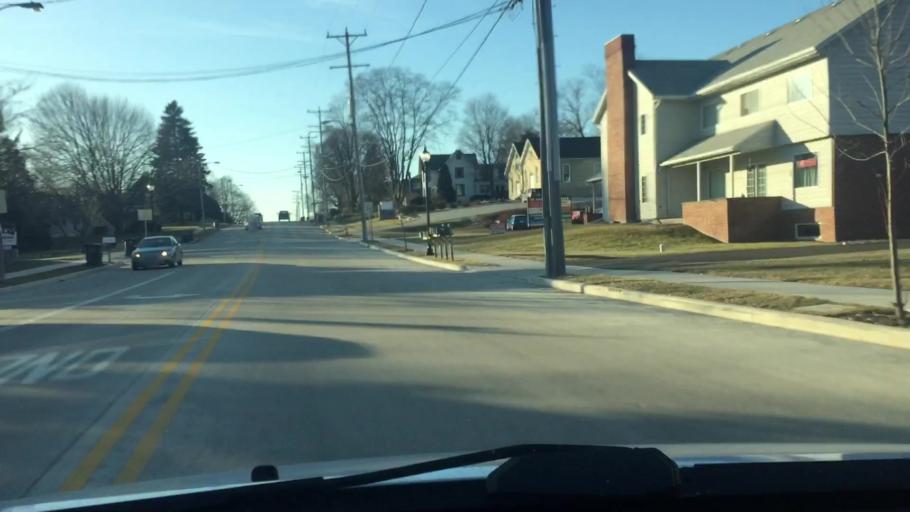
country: US
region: Wisconsin
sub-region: Waukesha County
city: Sussex
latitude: 43.1338
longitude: -88.2245
